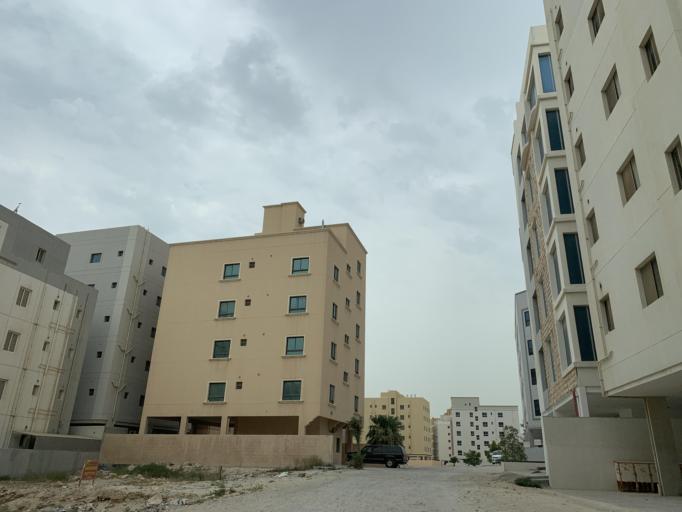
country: BH
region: Northern
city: Madinat `Isa
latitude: 26.1834
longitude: 50.4801
